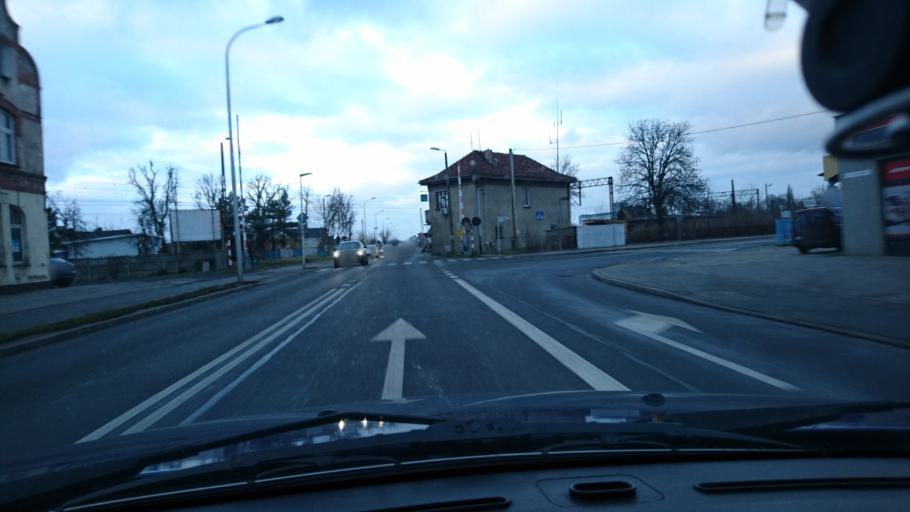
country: PL
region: Greater Poland Voivodeship
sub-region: Powiat kepinski
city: Kepno
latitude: 51.2895
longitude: 17.9938
